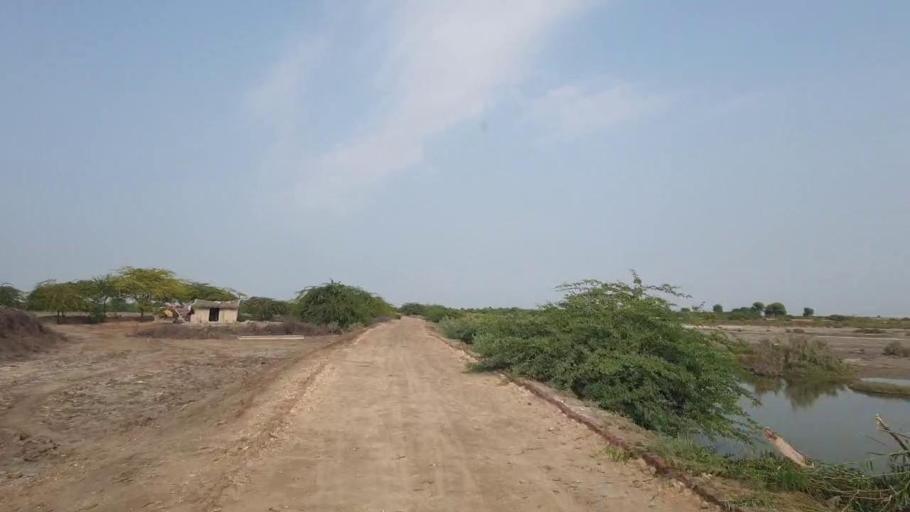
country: PK
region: Sindh
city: Kadhan
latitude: 24.4424
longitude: 68.7995
